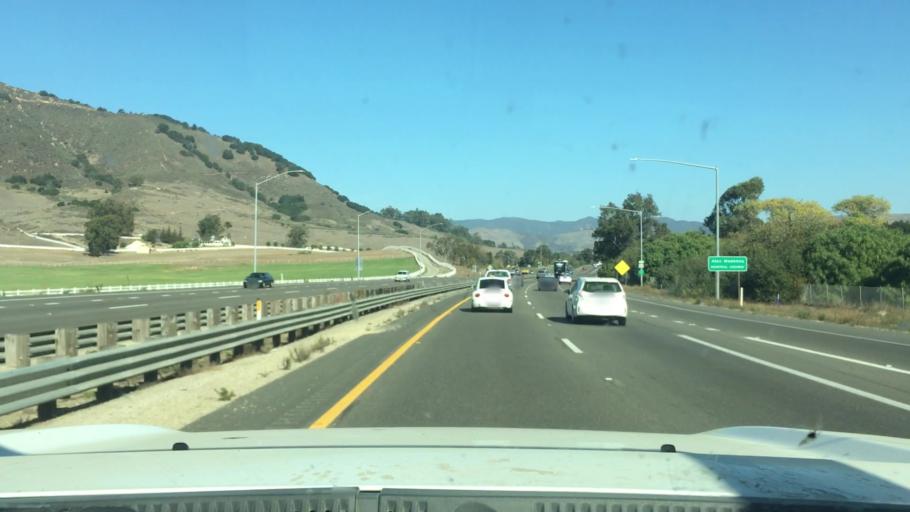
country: US
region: California
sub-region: San Luis Obispo County
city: San Luis Obispo
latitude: 35.2689
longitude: -120.6738
